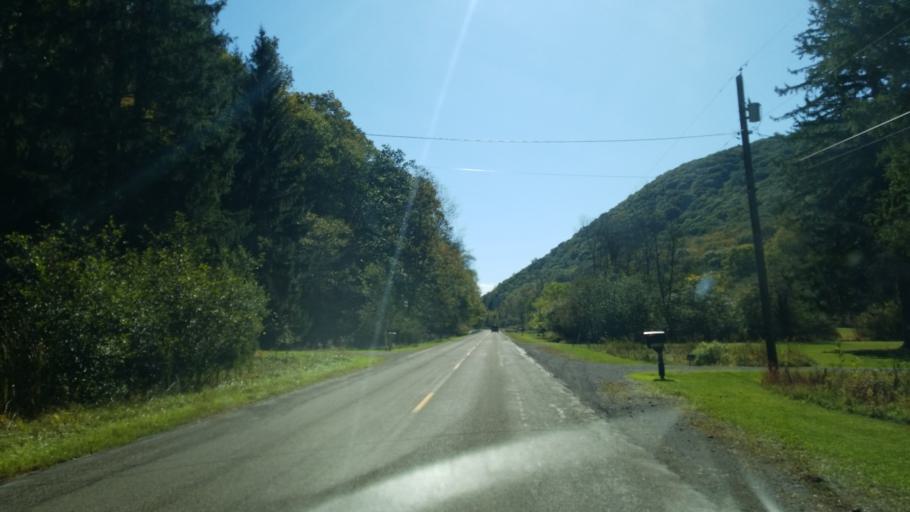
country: US
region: Pennsylvania
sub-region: Elk County
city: Saint Marys
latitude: 41.2786
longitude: -78.3988
